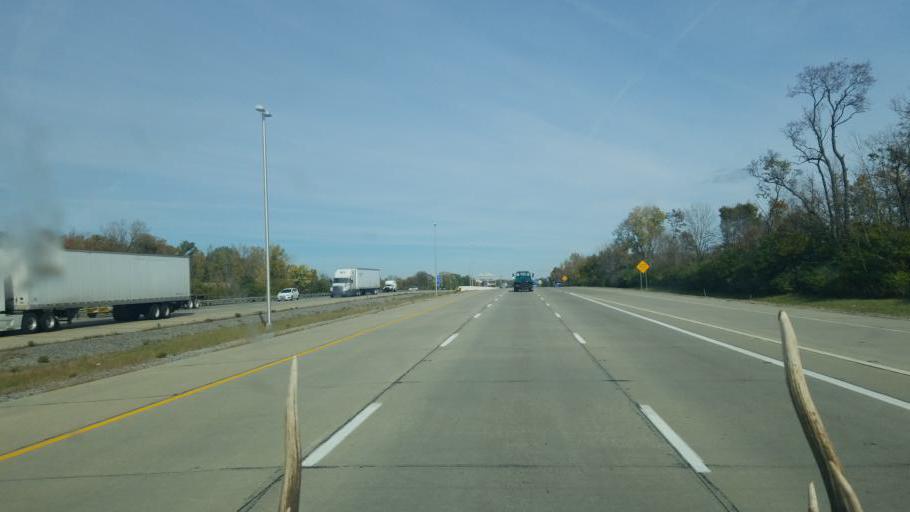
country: US
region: Indiana
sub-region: Marion County
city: Speedway
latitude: 39.7169
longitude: -86.2583
